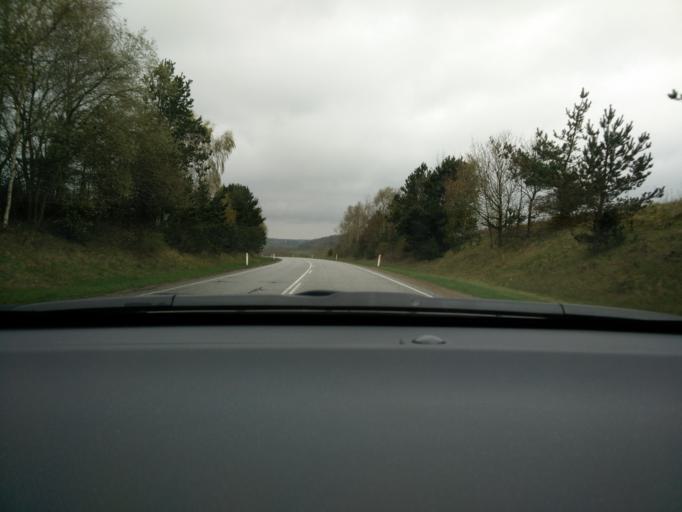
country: DK
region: Central Jutland
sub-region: Viborg Kommune
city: Viborg
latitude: 56.5085
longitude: 9.3239
